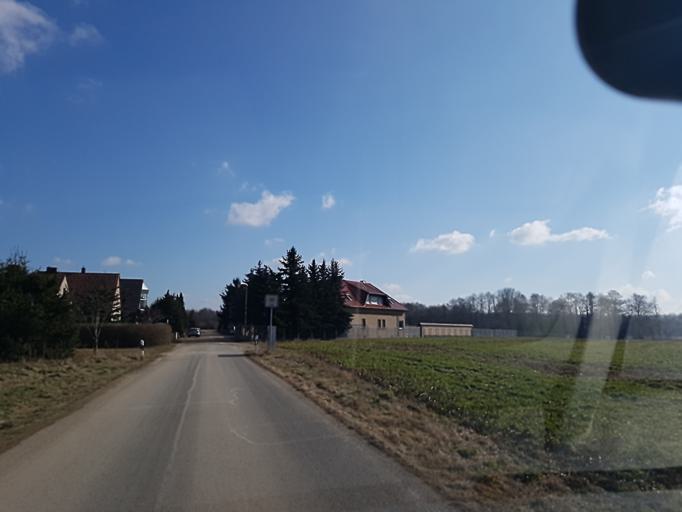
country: DE
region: Brandenburg
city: Doberlug-Kirchhain
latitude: 51.6039
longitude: 13.5542
